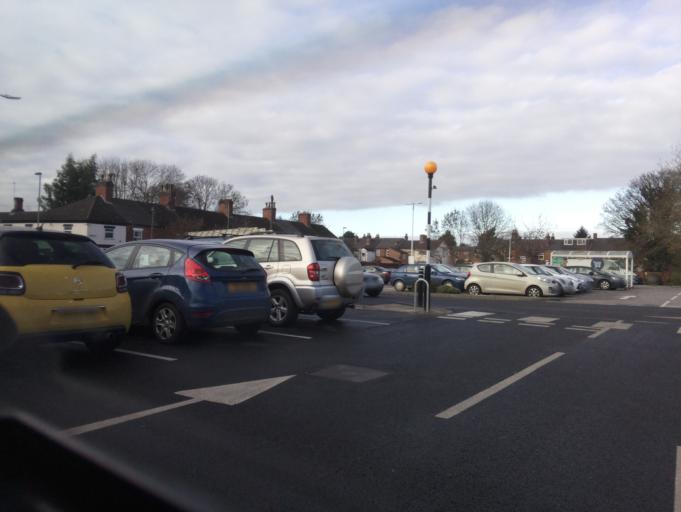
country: GB
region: England
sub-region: Staffordshire
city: Burton upon Trent
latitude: 52.7968
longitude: -1.6350
